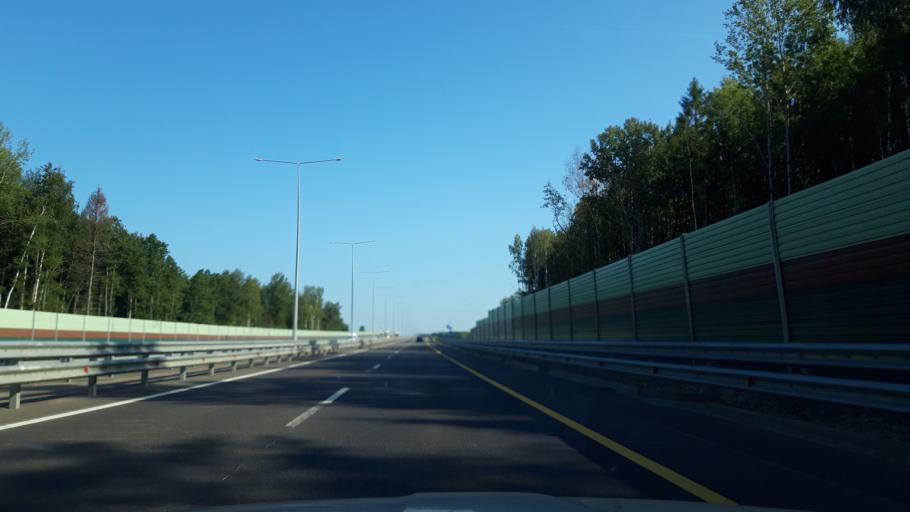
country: RU
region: Moskovskaya
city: Reshetnikovo
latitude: 56.4533
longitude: 36.5410
